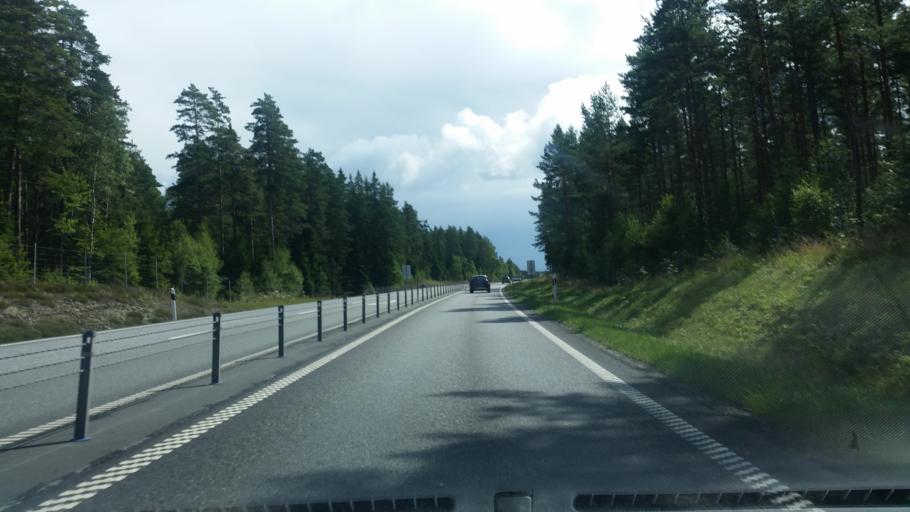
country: SE
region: Joenkoeping
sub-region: Mullsjo Kommun
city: Mullsjoe
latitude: 57.7689
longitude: 13.8061
